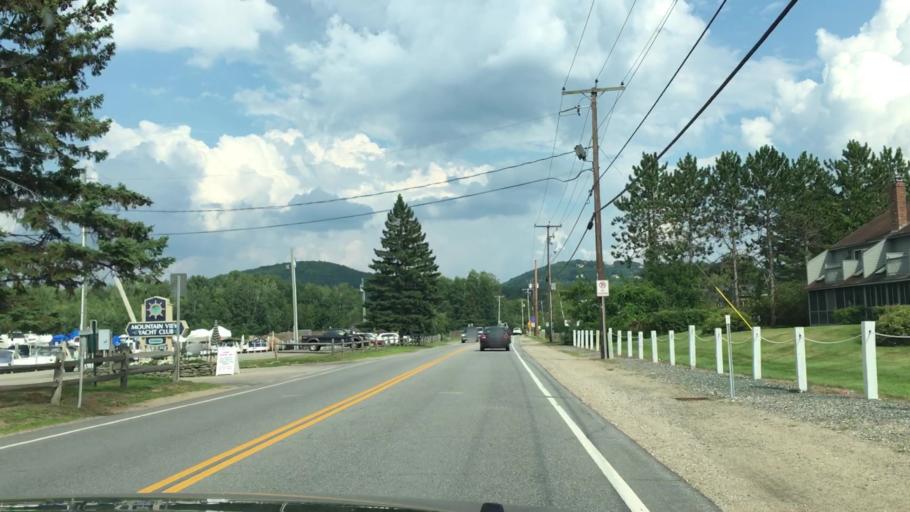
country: US
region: New Hampshire
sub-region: Belknap County
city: Gilford
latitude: 43.5790
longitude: -71.4058
